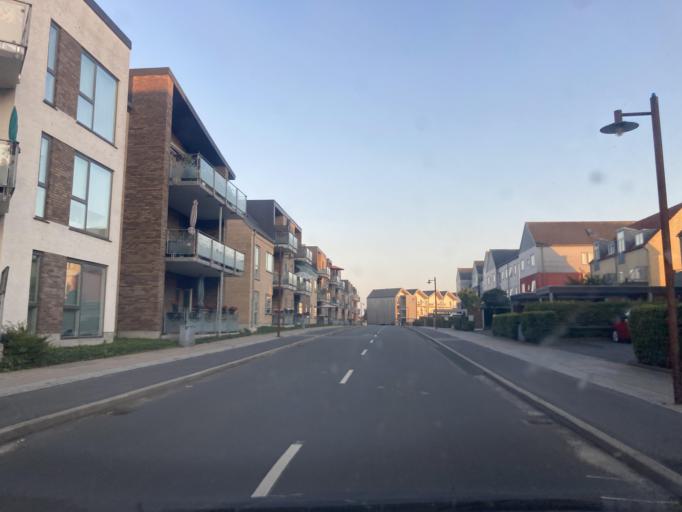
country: DK
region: South Denmark
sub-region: Nyborg Kommune
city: Nyborg
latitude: 55.3083
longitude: 10.7949
